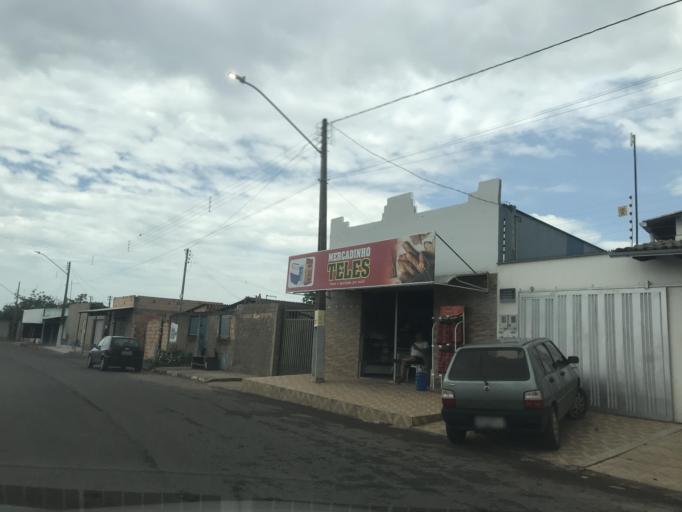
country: BR
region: Goias
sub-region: Luziania
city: Luziania
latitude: -16.2582
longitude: -47.9754
